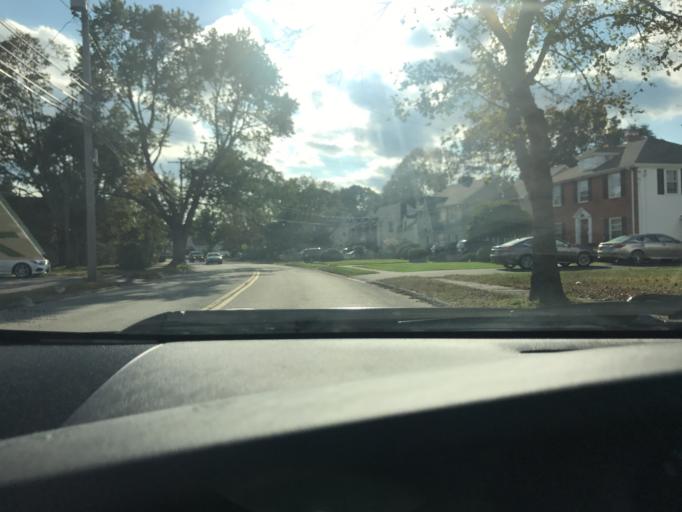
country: US
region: Massachusetts
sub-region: Middlesex County
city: Watertown
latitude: 42.3791
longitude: -71.2058
